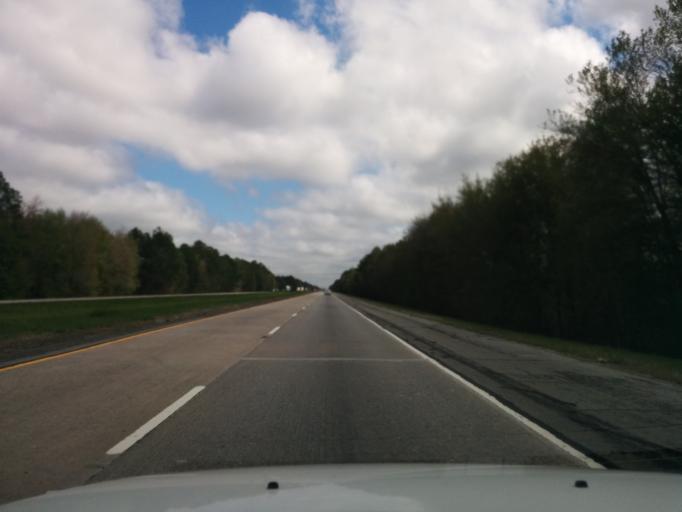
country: US
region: Georgia
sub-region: Chatham County
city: Bloomingdale
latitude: 32.1182
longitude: -81.3751
